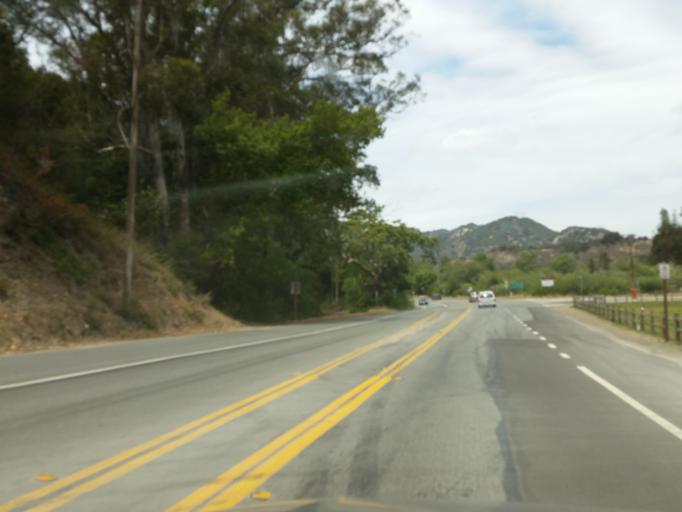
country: US
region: California
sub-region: San Luis Obispo County
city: Avila Beach
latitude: 35.1804
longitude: -120.7034
